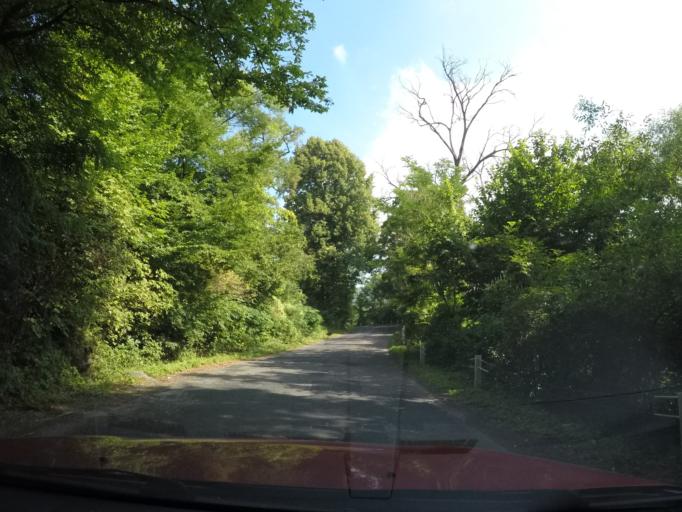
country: UA
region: Zakarpattia
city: Velykyi Bereznyi
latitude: 48.9151
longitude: 22.4589
